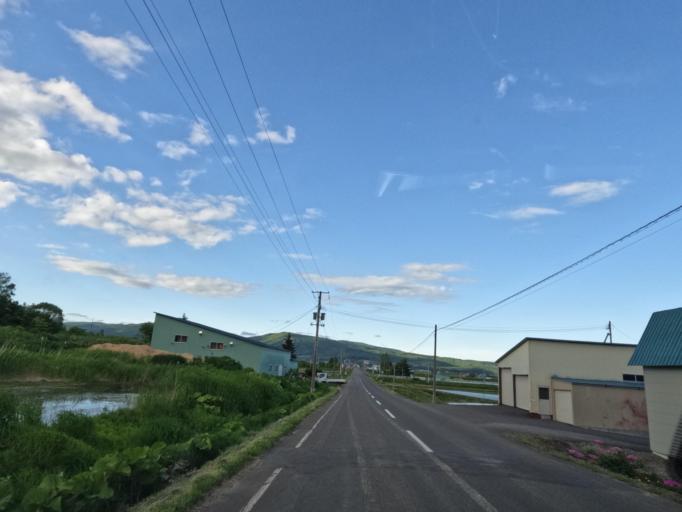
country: JP
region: Hokkaido
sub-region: Asahikawa-shi
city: Asahikawa
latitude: 43.8847
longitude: 142.4588
